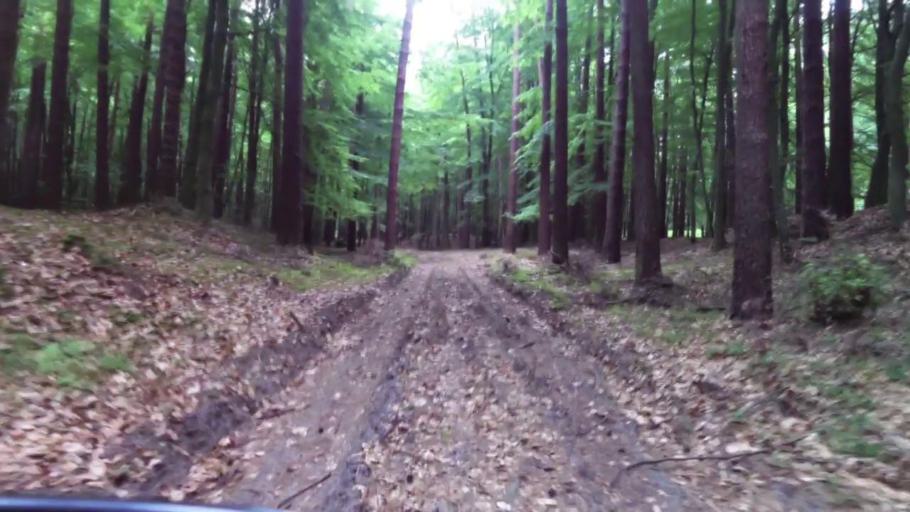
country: PL
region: West Pomeranian Voivodeship
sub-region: Powiat kamienski
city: Miedzyzdroje
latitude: 53.8728
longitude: 14.5032
